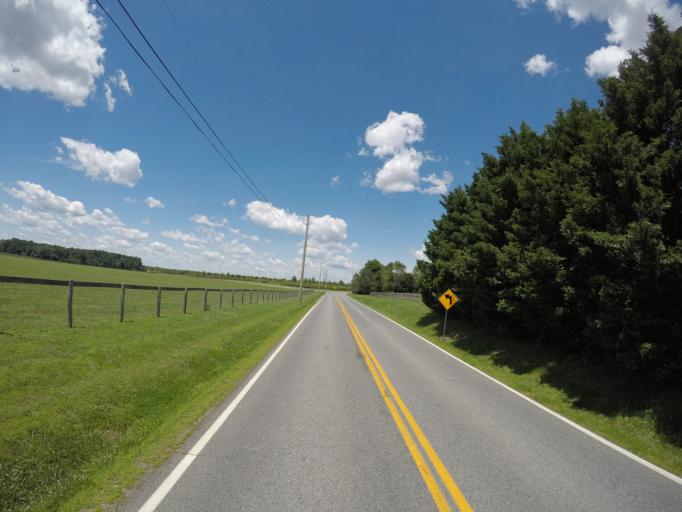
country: US
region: Delaware
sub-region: New Castle County
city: Middletown
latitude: 39.4752
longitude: -75.7794
